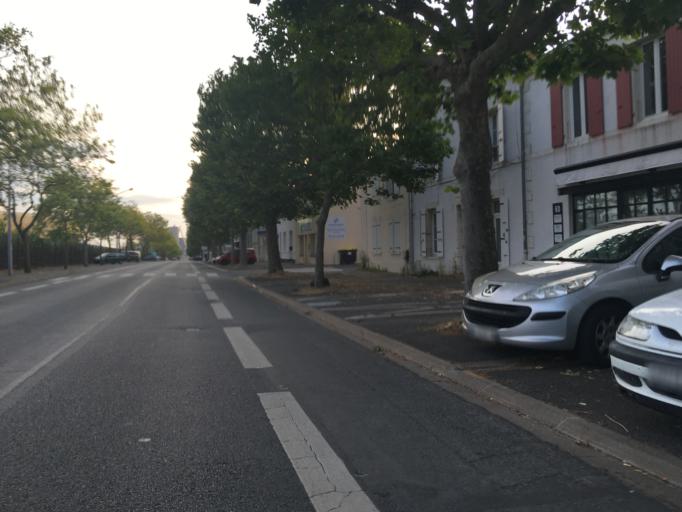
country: FR
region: Poitou-Charentes
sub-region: Departement de la Charente-Maritime
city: Rivedoux-Plage
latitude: 46.1611
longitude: -1.2119
